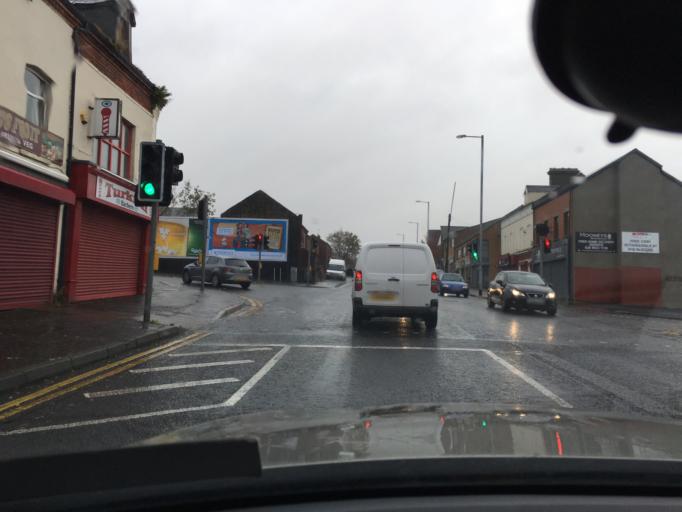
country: GB
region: Northern Ireland
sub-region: City of Belfast
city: Belfast
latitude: 54.6233
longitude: -5.9761
